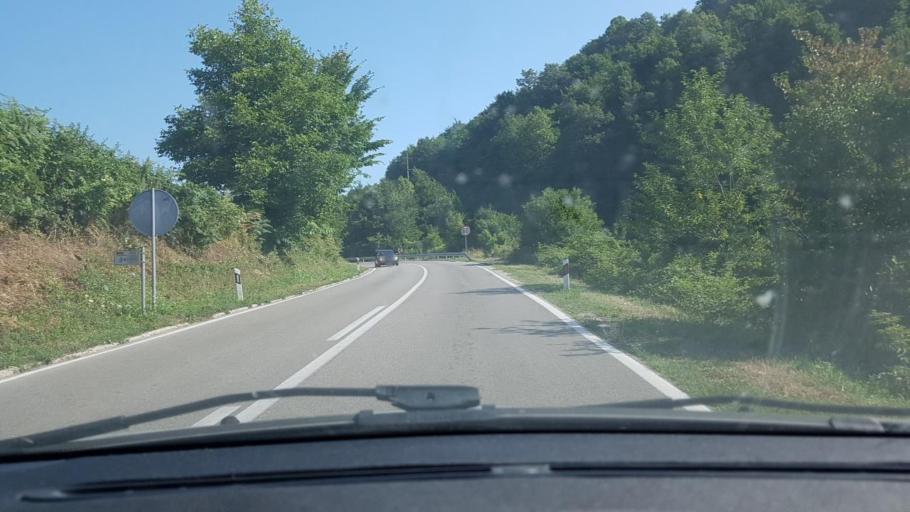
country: BA
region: Federation of Bosnia and Herzegovina
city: Skokovi
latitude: 45.0159
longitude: 15.9039
